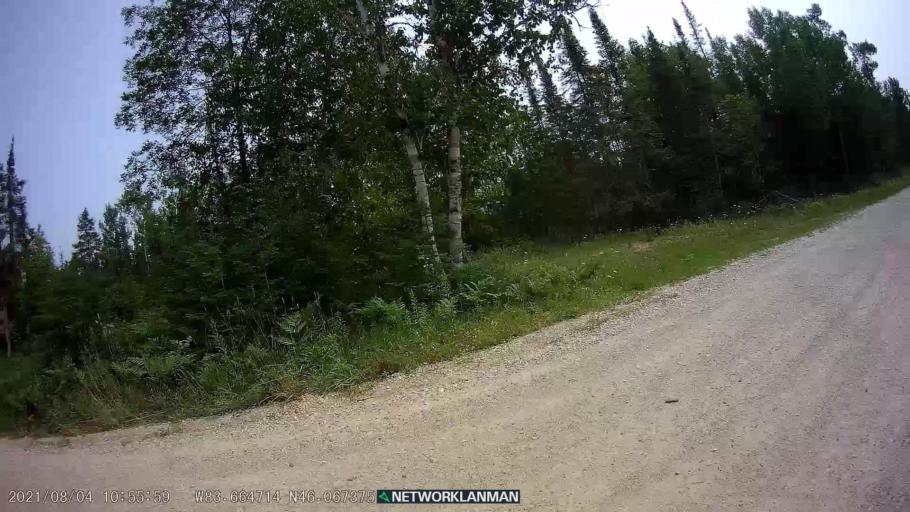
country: CA
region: Ontario
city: Thessalon
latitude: 46.0672
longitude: -83.6652
